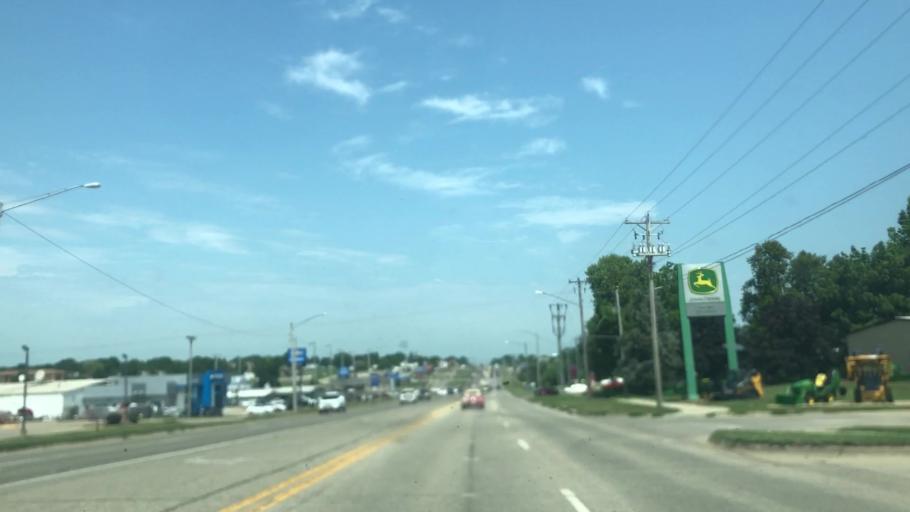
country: US
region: Iowa
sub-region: Marshall County
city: Marshalltown
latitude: 42.0093
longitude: -92.9123
